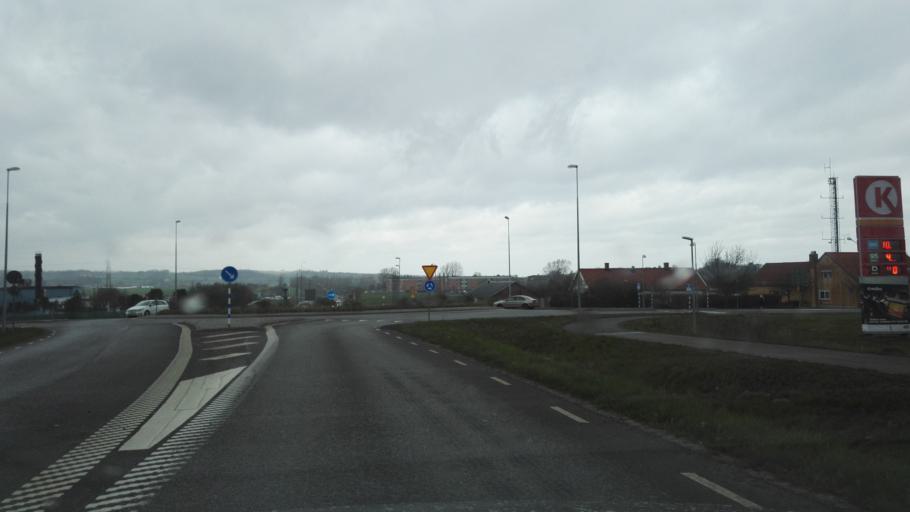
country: SE
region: Skane
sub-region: Simrishamns Kommun
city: Simrishamn
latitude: 55.5462
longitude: 14.3356
